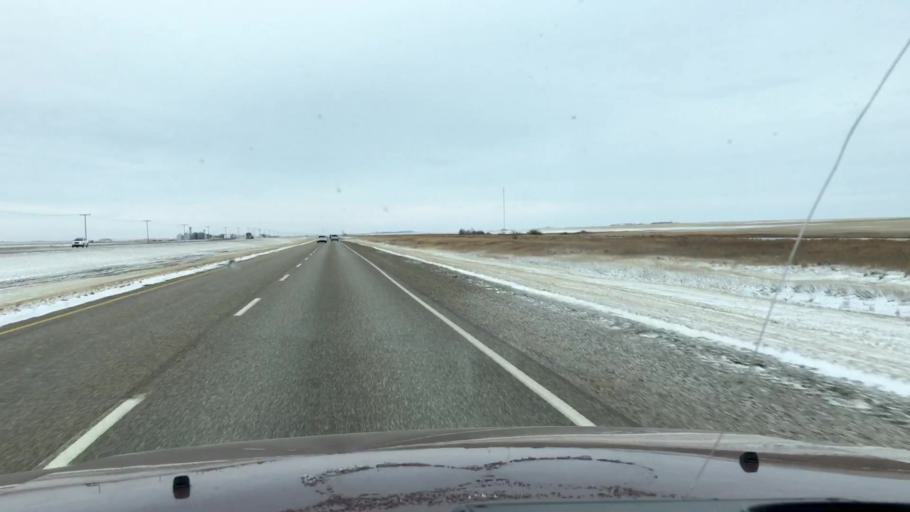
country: CA
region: Saskatchewan
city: Moose Jaw
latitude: 51.0225
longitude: -105.7889
